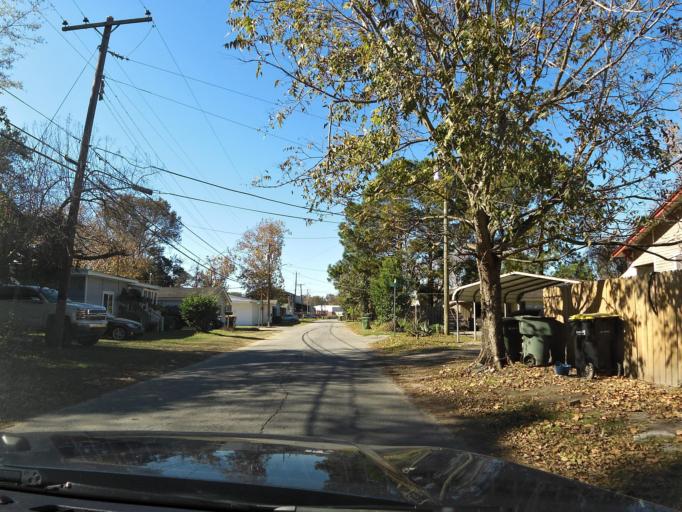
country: US
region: Georgia
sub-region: Chatham County
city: Savannah
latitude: 32.0749
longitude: -81.1198
